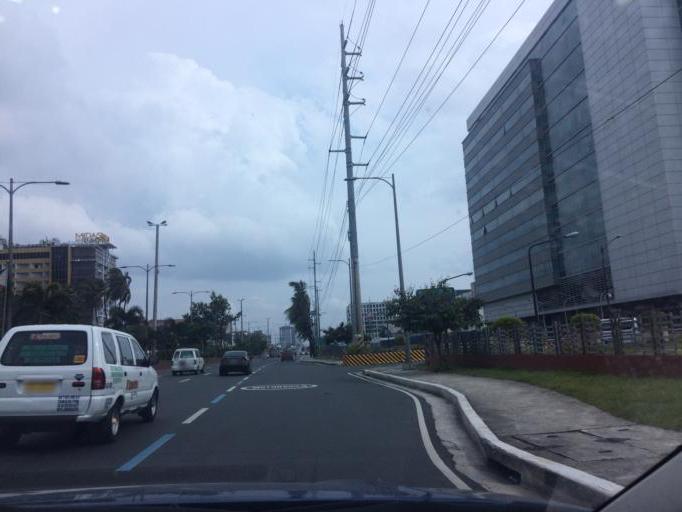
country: PH
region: Metro Manila
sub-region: Makati City
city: Makati City
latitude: 14.5414
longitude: 120.9918
